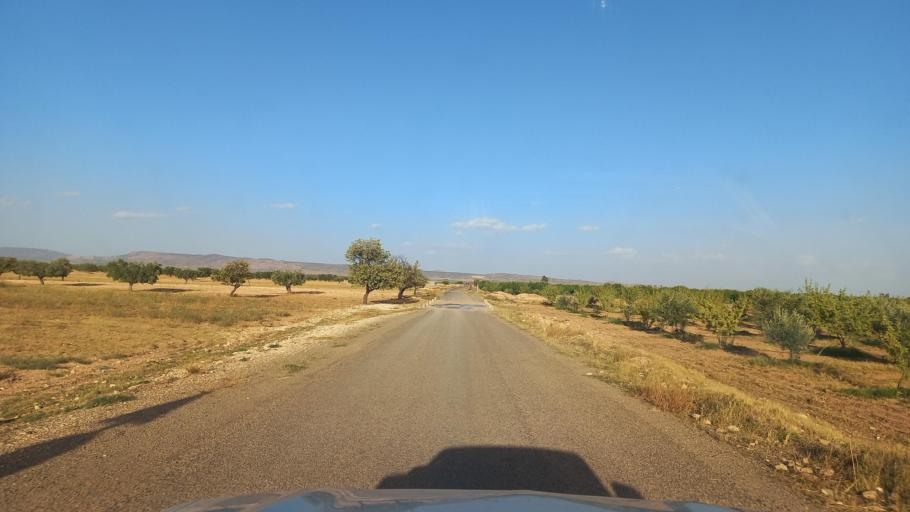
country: TN
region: Al Qasrayn
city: Kasserine
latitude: 35.2867
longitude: 9.0278
